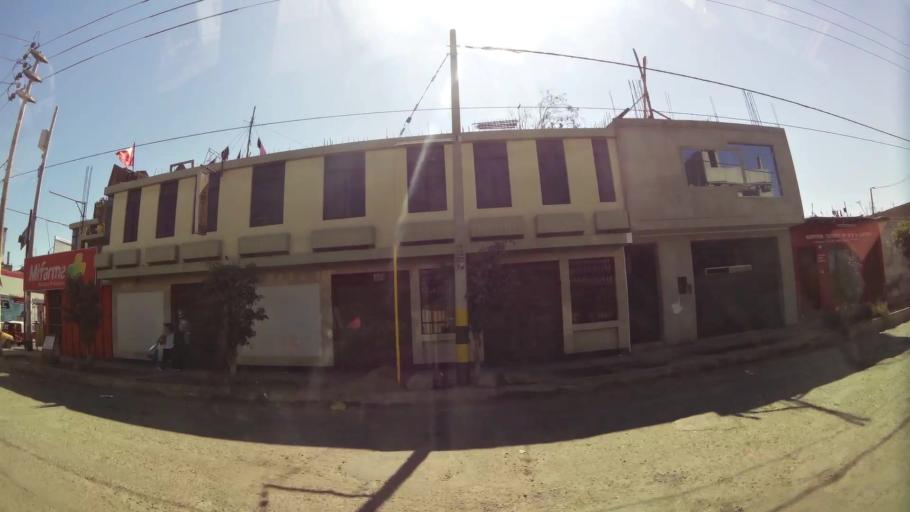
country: PE
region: Ica
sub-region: Provincia de Ica
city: La Tinguina
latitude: -14.0499
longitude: -75.7026
